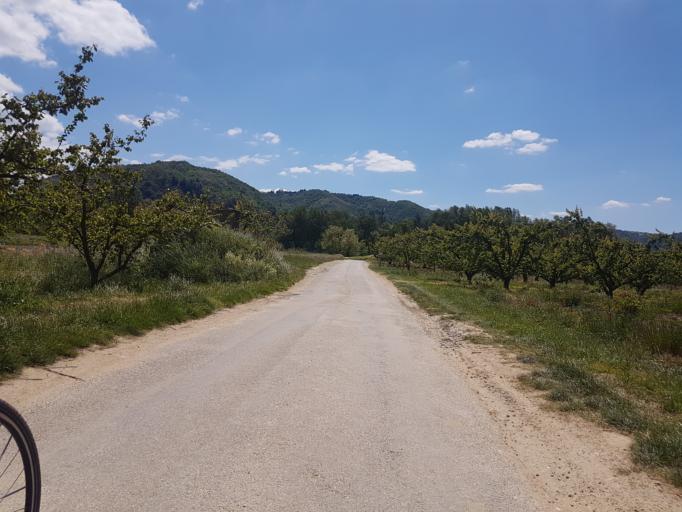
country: FR
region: Rhone-Alpes
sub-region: Departement de l'Ardeche
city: Saint-Jean-de-Muzols
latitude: 45.0800
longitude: 4.8225
